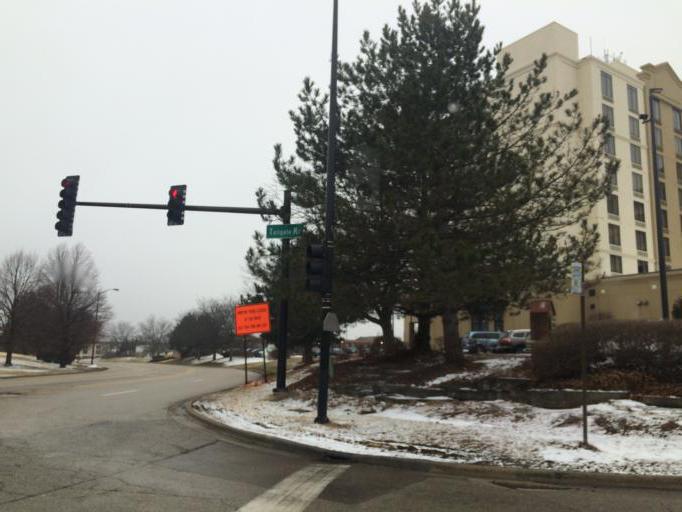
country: US
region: Illinois
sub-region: Kane County
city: Sleepy Hollow
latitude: 42.0730
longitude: -88.2886
